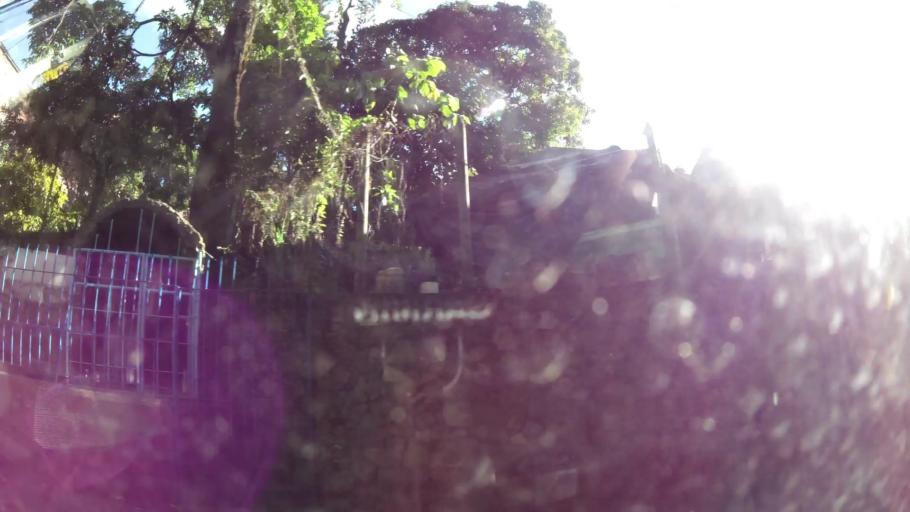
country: CO
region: Antioquia
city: Envigado
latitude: 6.1772
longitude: -75.5795
